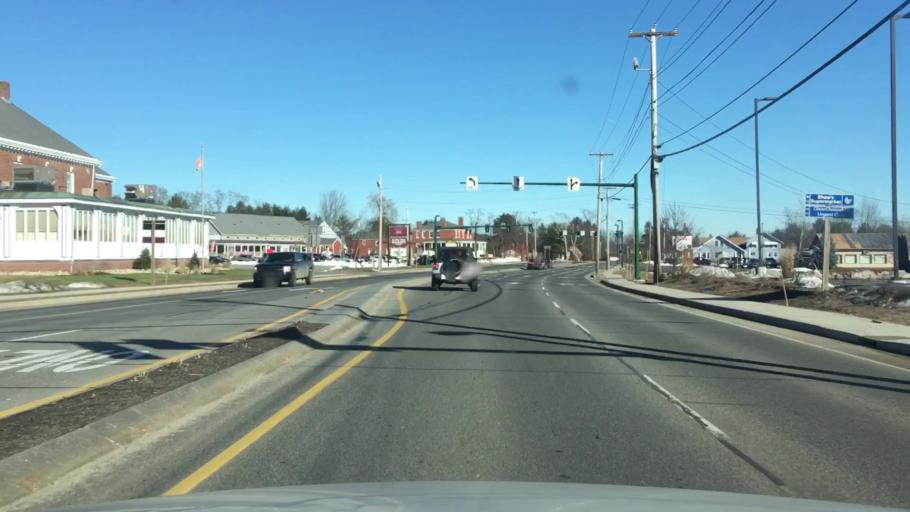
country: US
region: Maine
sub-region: Cumberland County
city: West Scarborough
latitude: 43.5718
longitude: -70.3868
